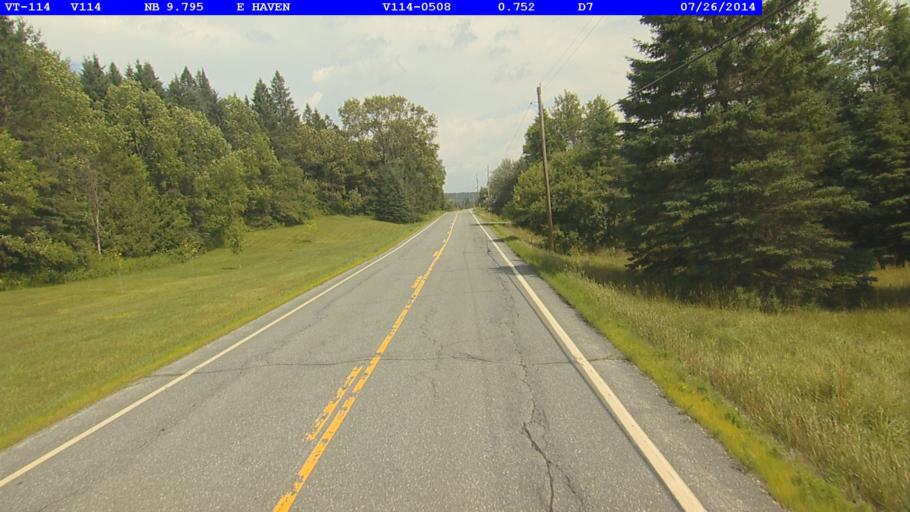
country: US
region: Vermont
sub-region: Caledonia County
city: Lyndonville
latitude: 44.6497
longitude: -71.8925
